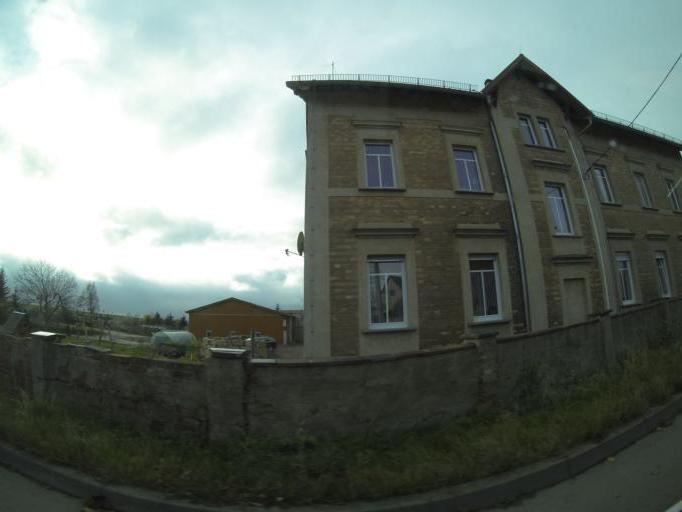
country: DE
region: Thuringia
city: Schmolln
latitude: 50.8841
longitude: 12.3855
